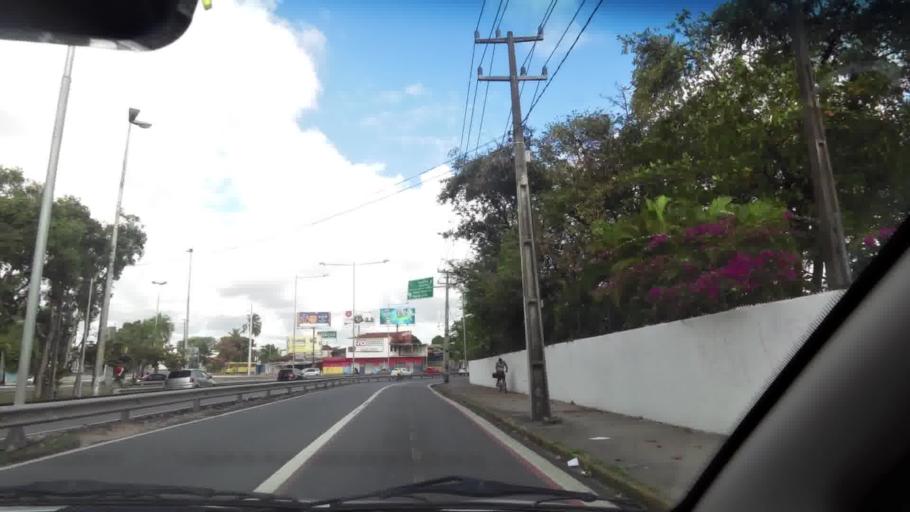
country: BR
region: Pernambuco
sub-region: Recife
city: Recife
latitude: -8.0803
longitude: -34.8915
